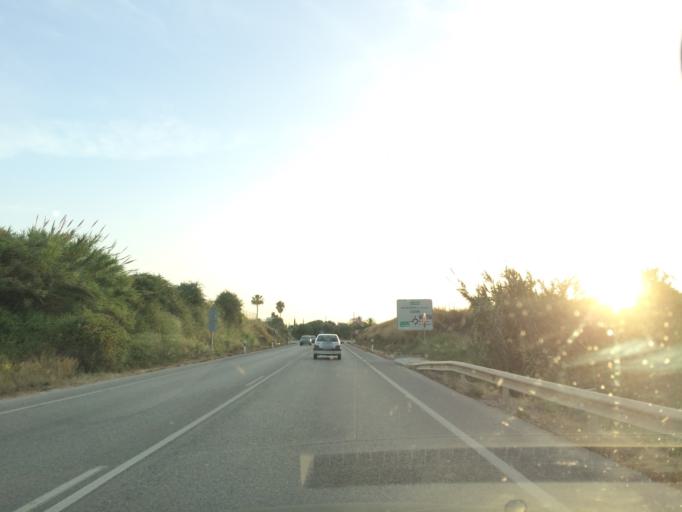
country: ES
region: Andalusia
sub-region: Provincia de Malaga
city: Alhaurin de la Torre
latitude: 36.6687
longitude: -4.5732
